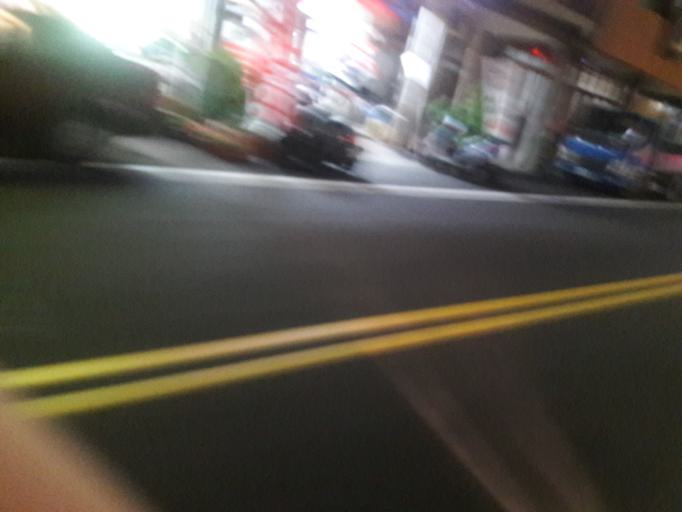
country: TW
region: Taiwan
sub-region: Miaoli
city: Miaoli
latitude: 24.4873
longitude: 120.6794
